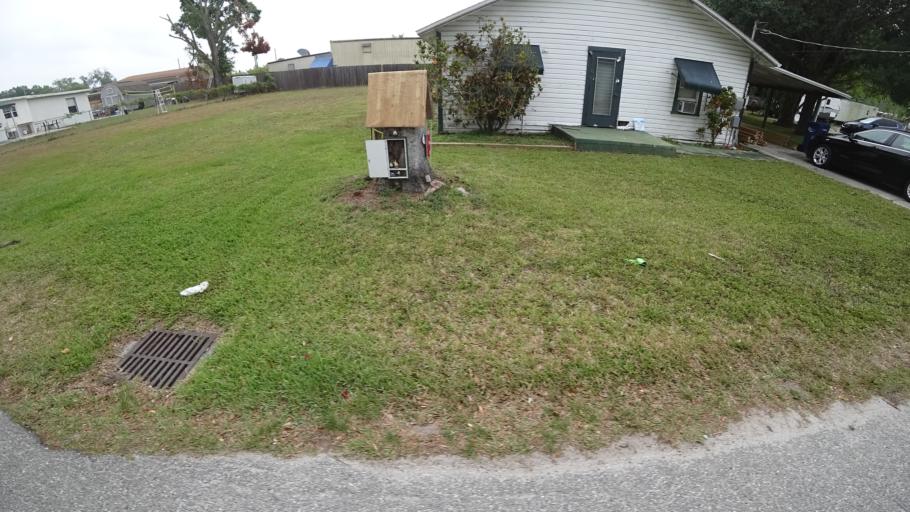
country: US
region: Florida
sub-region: Manatee County
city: West Samoset
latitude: 27.4742
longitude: -82.5512
